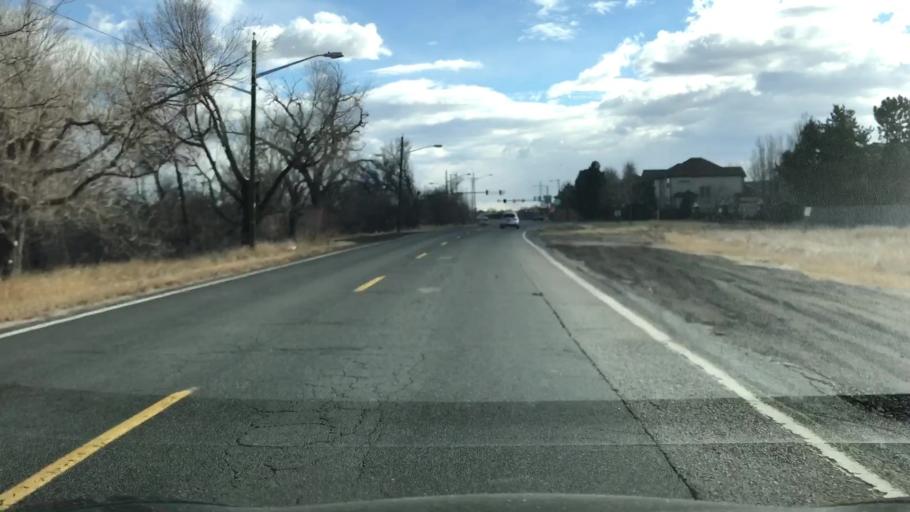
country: US
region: Colorado
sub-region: Arapahoe County
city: Glendale
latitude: 39.6863
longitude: -104.9056
